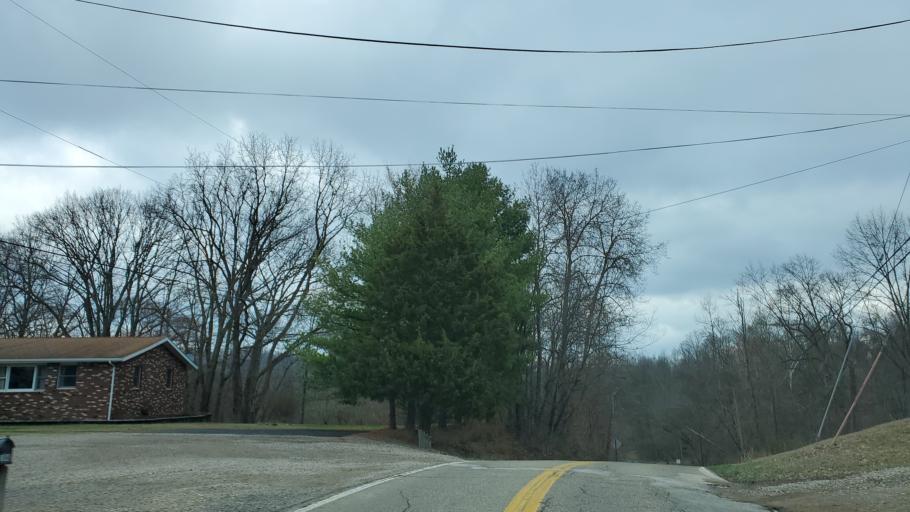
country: US
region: Ohio
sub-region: Licking County
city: Newark
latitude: 40.0394
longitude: -82.3741
